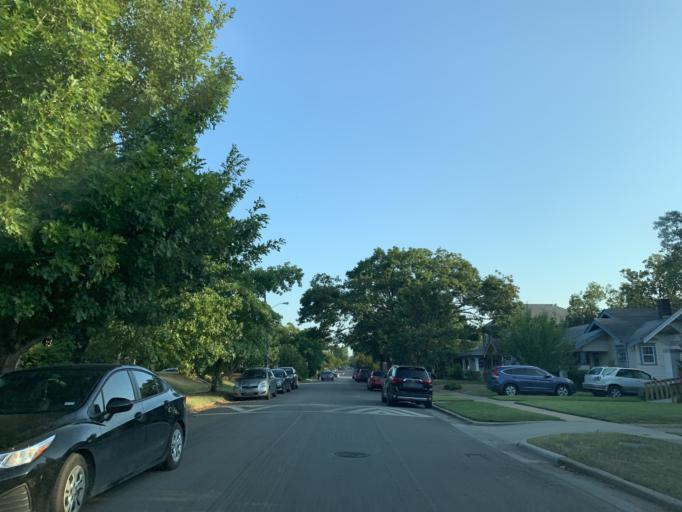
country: US
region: Texas
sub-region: Dallas County
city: Cockrell Hill
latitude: 32.7483
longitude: -96.8515
